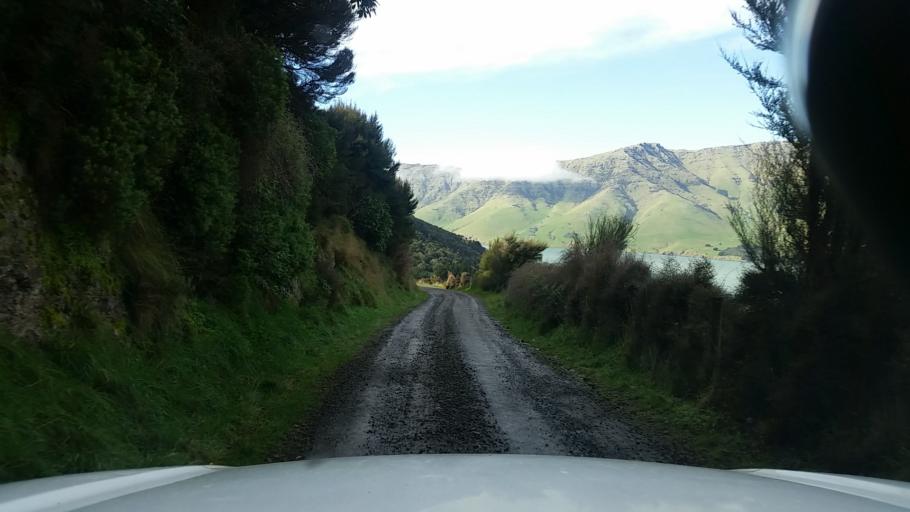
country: NZ
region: Canterbury
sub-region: Christchurch City
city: Christchurch
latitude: -43.6715
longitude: 172.8631
